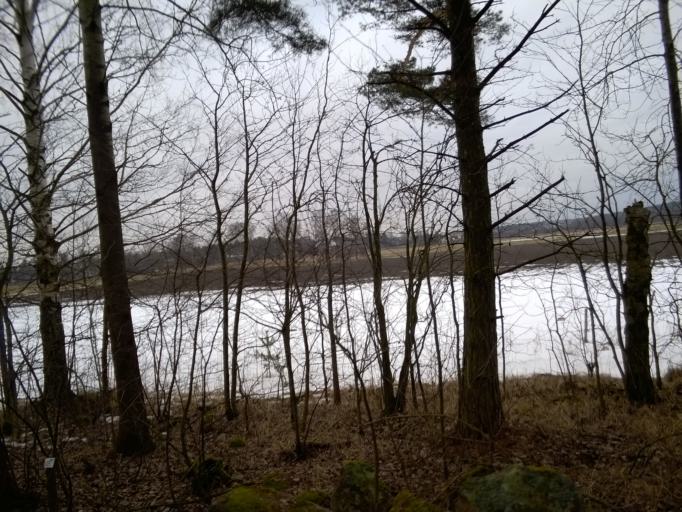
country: FI
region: Uusimaa
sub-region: Helsinki
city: Vantaa
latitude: 60.2154
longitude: 25.0139
